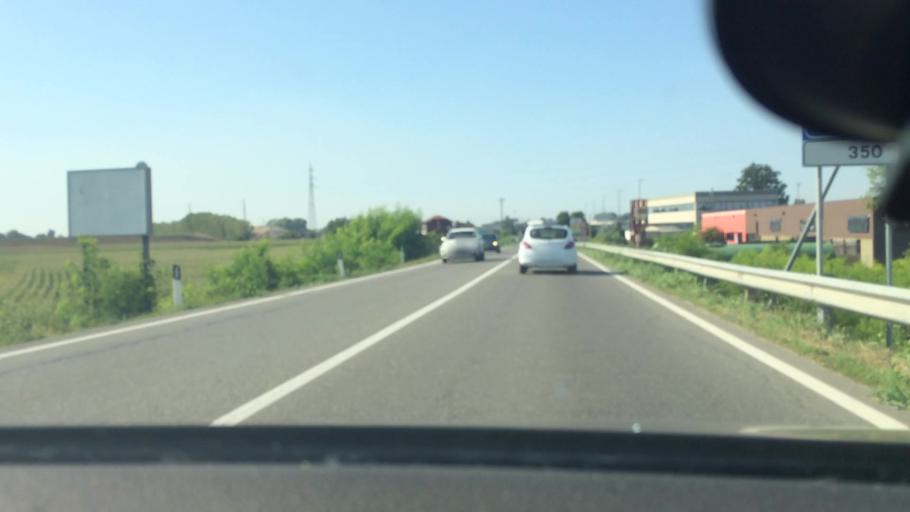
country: IT
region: Lombardy
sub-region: Provincia di Lodi
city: Guardamiglio
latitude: 45.0943
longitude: 9.6892
